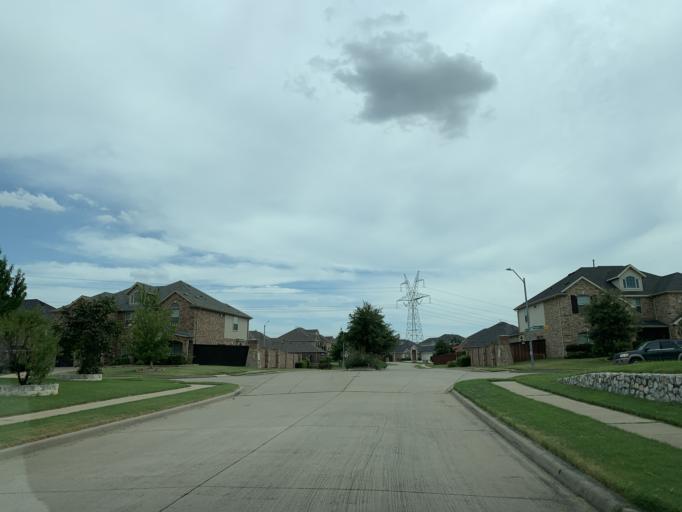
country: US
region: Texas
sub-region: Tarrant County
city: Arlington
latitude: 32.6550
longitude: -97.0459
